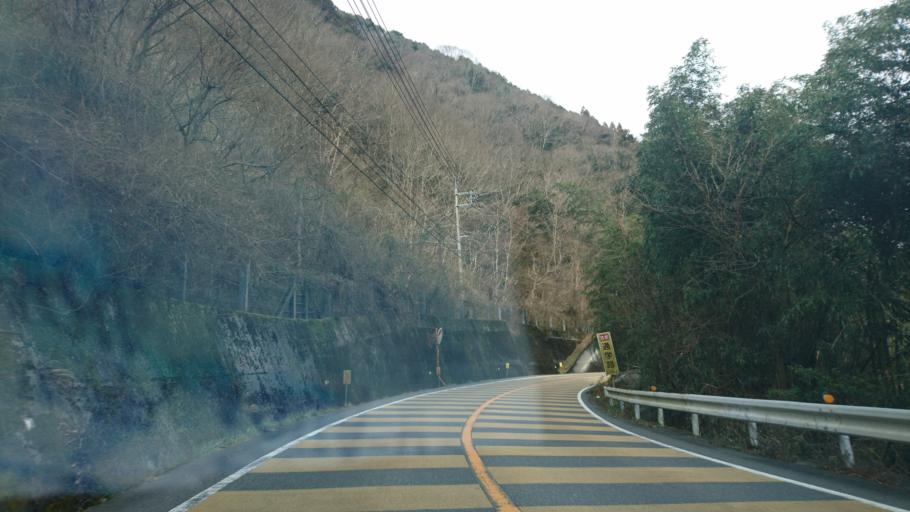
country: JP
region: Okayama
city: Takahashi
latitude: 34.8214
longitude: 133.6324
